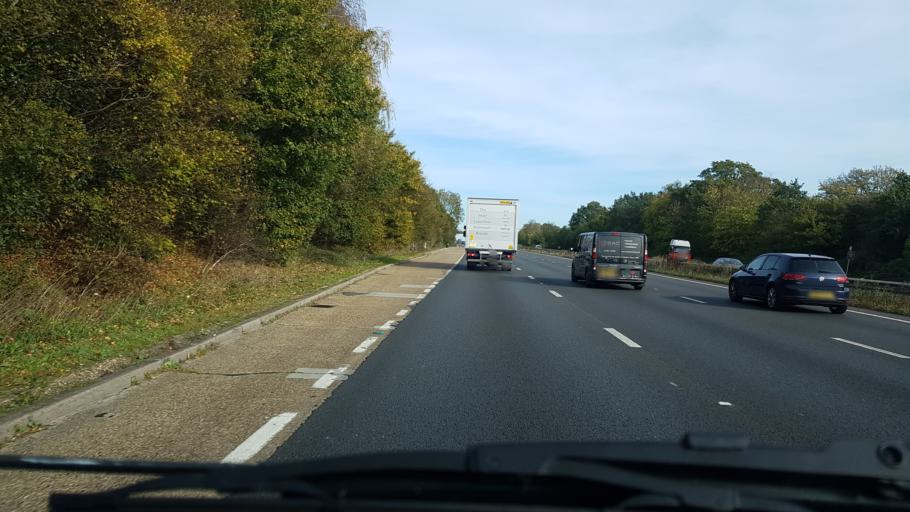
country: GB
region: England
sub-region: Surrey
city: Ripley
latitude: 51.2864
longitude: -0.4973
